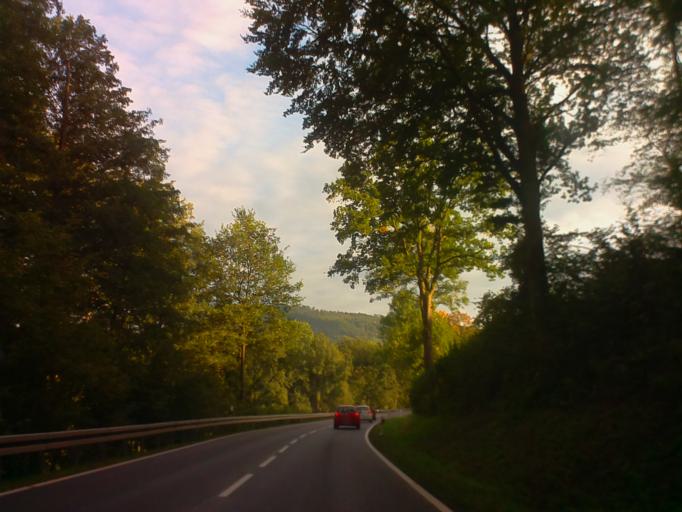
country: DE
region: Hesse
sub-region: Regierungsbezirk Darmstadt
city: Lindenfels
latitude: 49.6724
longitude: 8.8012
